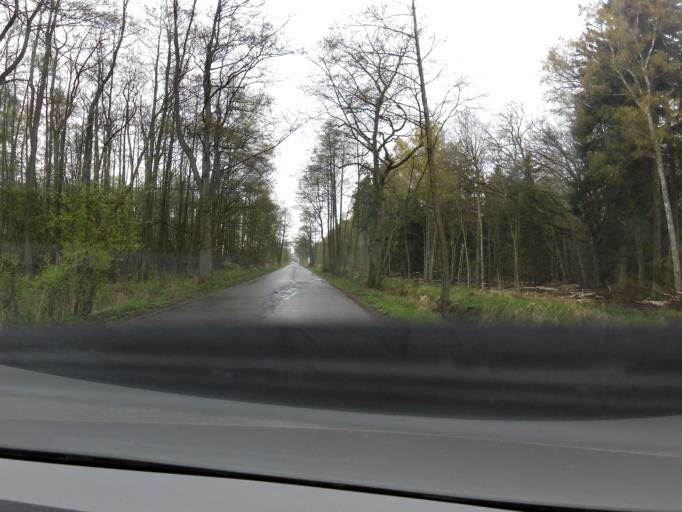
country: DE
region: Mecklenburg-Vorpommern
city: Barth
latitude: 54.4280
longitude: 12.8002
